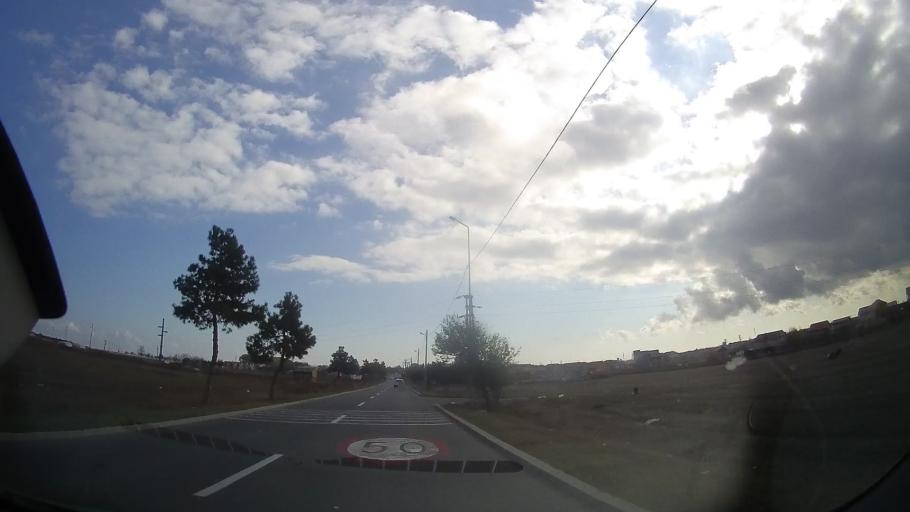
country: RO
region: Constanta
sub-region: Oras Techirghiol
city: Techirghiol
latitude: 44.0648
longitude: 28.5941
